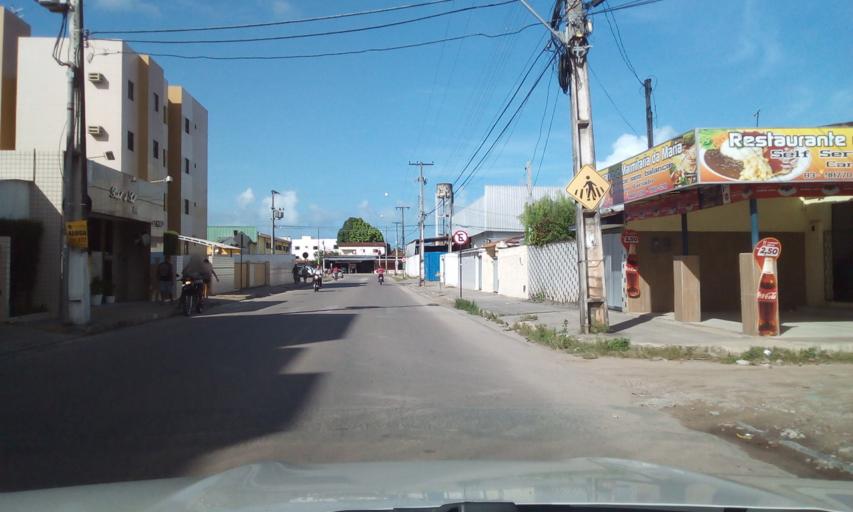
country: BR
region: Paraiba
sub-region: Joao Pessoa
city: Joao Pessoa
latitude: -7.1776
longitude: -34.8750
